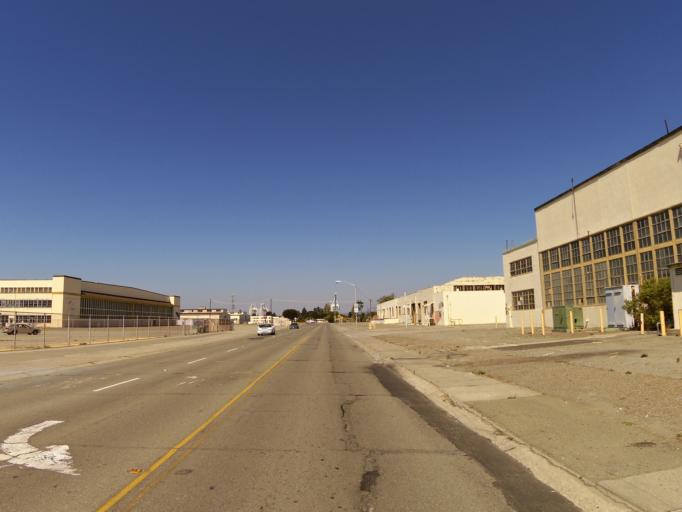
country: US
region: California
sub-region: Alameda County
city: Oakland
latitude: 37.7802
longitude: -122.2980
